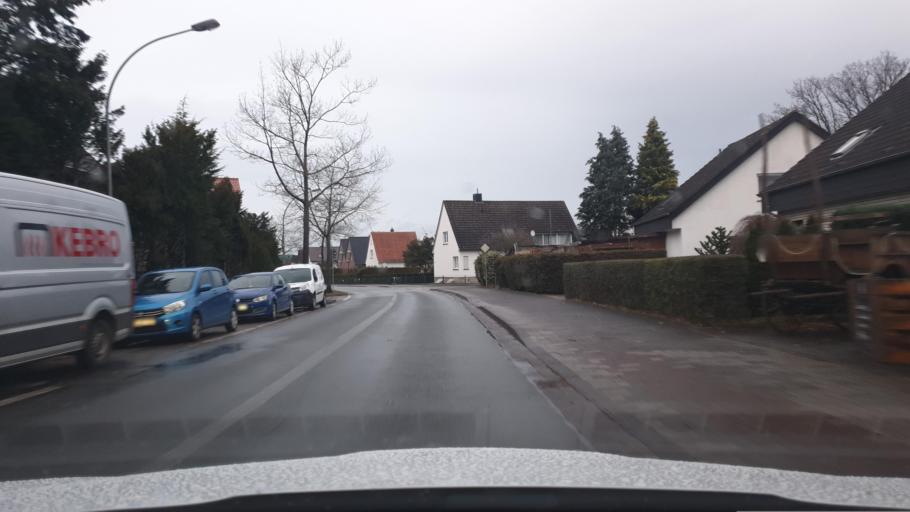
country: DE
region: North Rhine-Westphalia
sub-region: Regierungsbezirk Detmold
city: Lage
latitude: 51.9489
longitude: 8.8117
